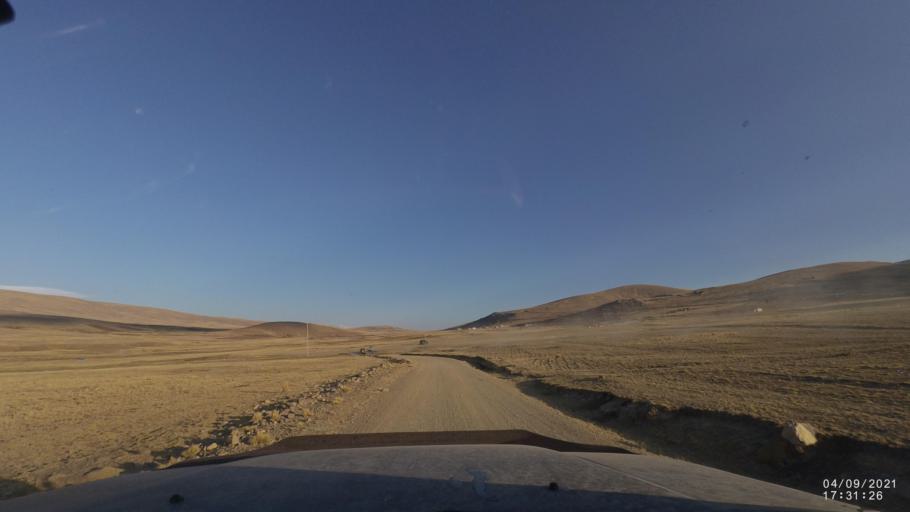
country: BO
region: Cochabamba
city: Cochabamba
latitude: -17.2423
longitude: -66.2320
